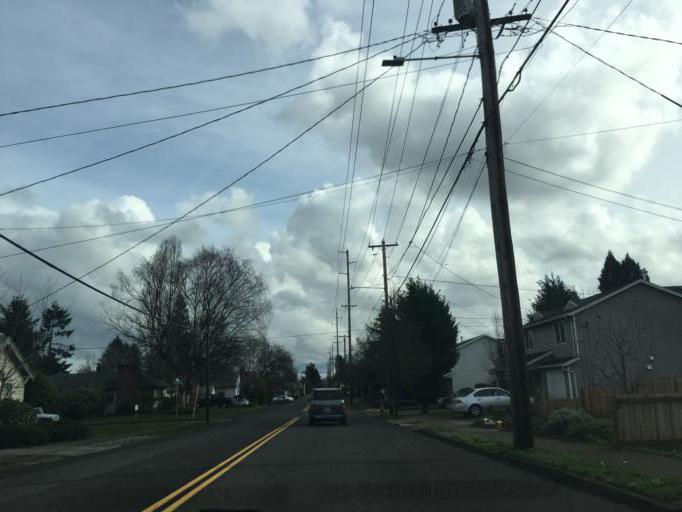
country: US
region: Oregon
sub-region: Multnomah County
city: Lents
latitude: 45.4903
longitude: -122.6127
